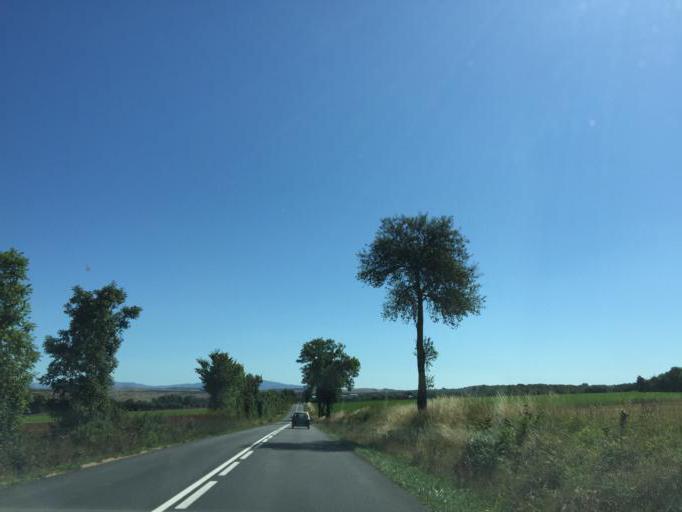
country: FR
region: Midi-Pyrenees
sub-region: Departement de l'Aveyron
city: La Cavalerie
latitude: 44.0154
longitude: 3.1010
